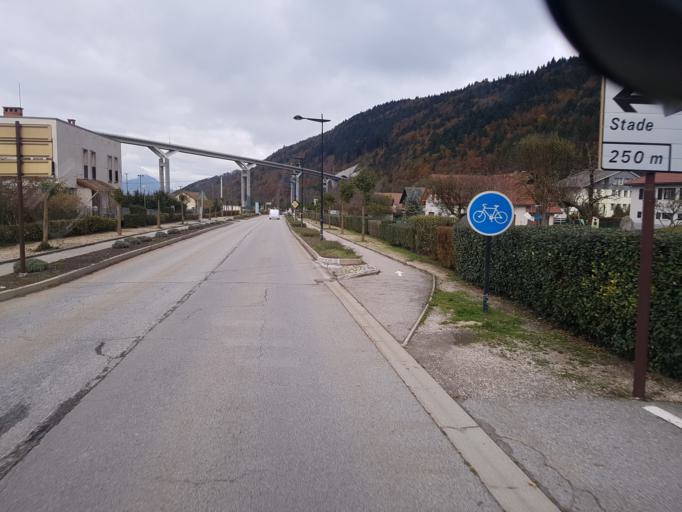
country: FR
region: Rhone-Alpes
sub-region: Departement de l'Isere
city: La Motte-Saint-Martin
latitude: 44.9268
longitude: 5.6384
